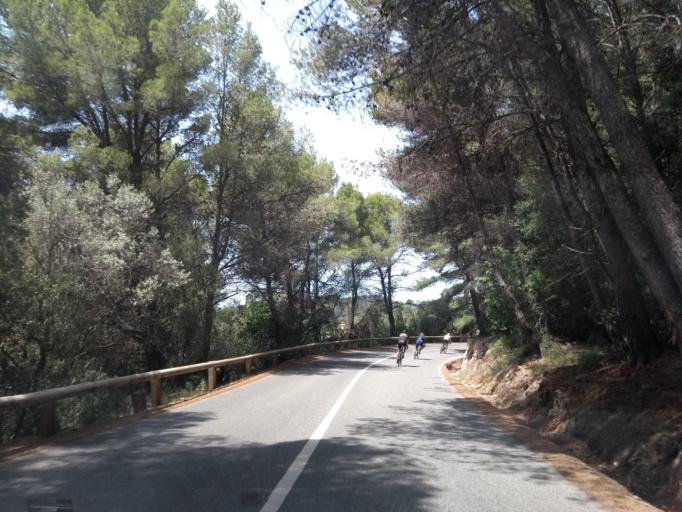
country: ES
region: Balearic Islands
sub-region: Illes Balears
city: Soller
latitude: 39.7788
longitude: 2.7184
